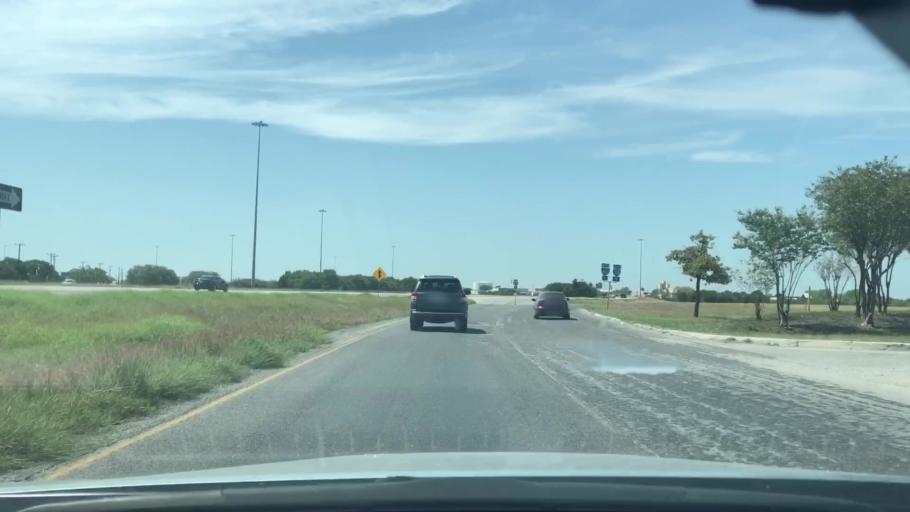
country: US
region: Texas
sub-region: Bexar County
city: Kirby
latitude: 29.4561
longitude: -98.4046
